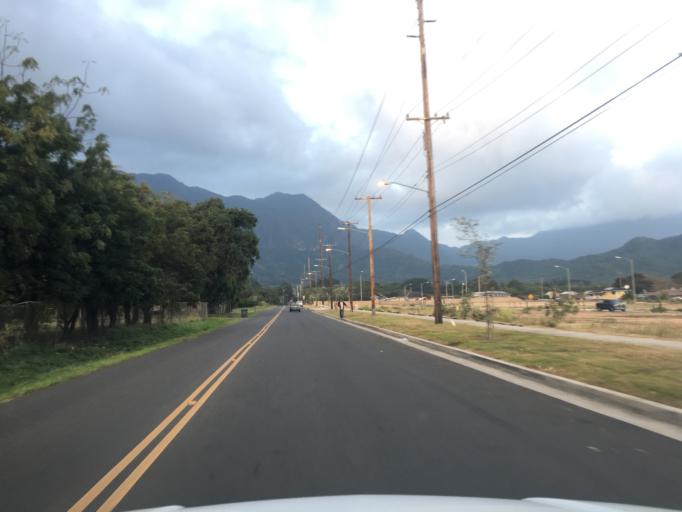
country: US
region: Hawaii
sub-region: Honolulu County
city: Waimanalo
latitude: 21.3445
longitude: -157.7231
